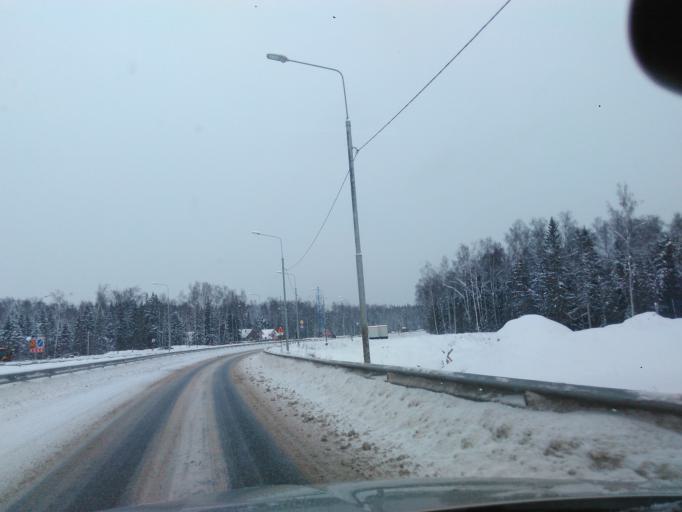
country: RU
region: Moskovskaya
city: Povarovo
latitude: 56.0083
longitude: 37.0283
